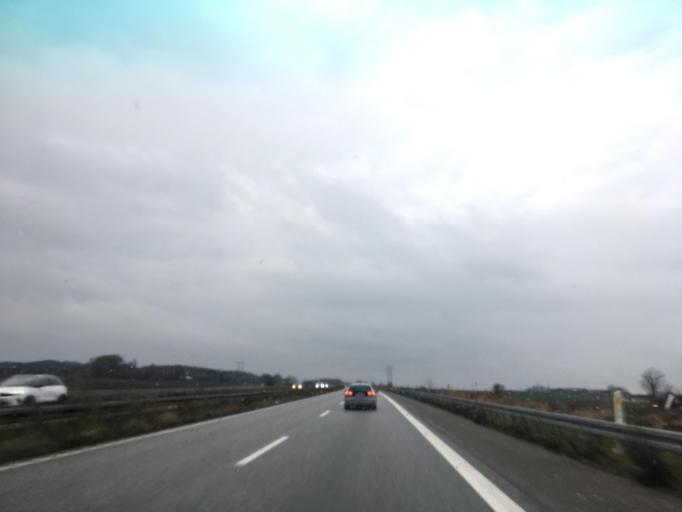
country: DK
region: Zealand
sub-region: Guldborgsund Kommune
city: Norre Alslev
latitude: 54.8740
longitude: 11.8920
